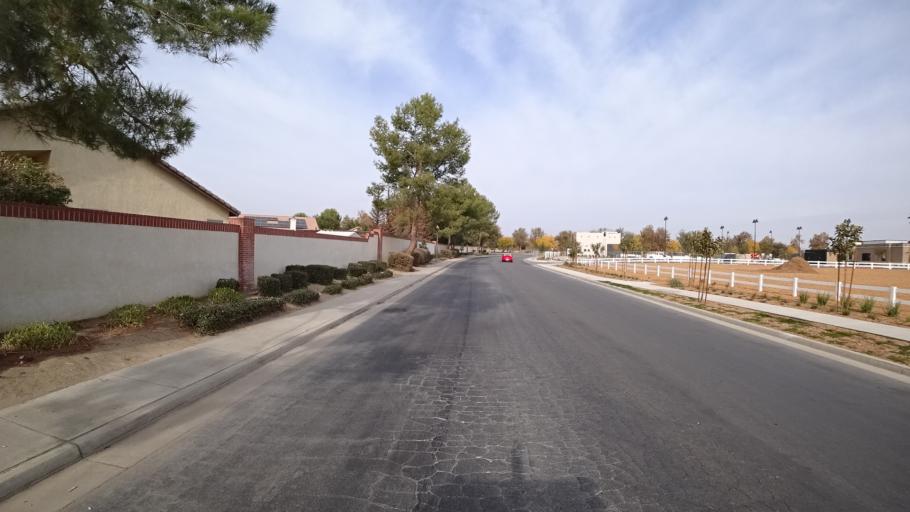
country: US
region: California
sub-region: Kern County
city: Rosedale
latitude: 35.3484
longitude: -119.1299
